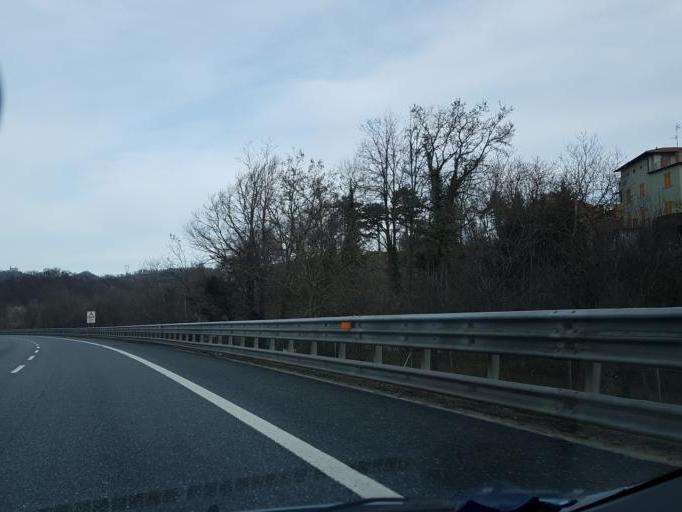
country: IT
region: Piedmont
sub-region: Provincia di Alessandria
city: Arquata Scrivia
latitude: 44.6896
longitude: 8.9008
